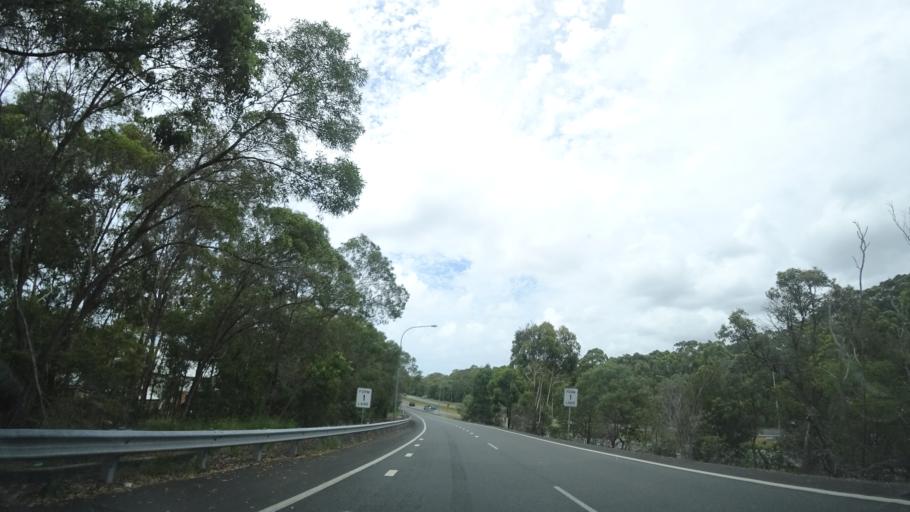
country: AU
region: Queensland
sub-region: Sunshine Coast
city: Mooloolaba
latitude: -26.6754
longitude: 153.0977
